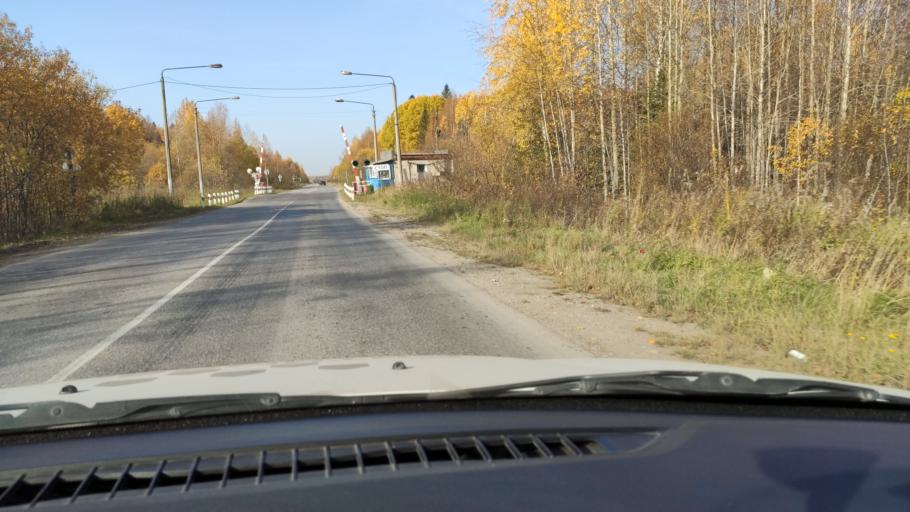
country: RU
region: Perm
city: Novyye Lyady
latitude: 58.0286
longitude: 56.6248
